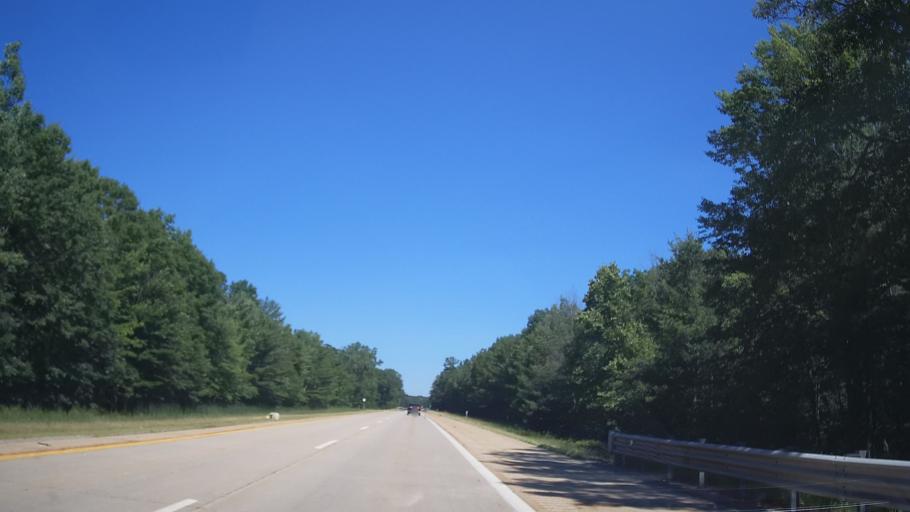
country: US
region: Michigan
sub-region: Midland County
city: Coleman
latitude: 43.7038
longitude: -84.4426
